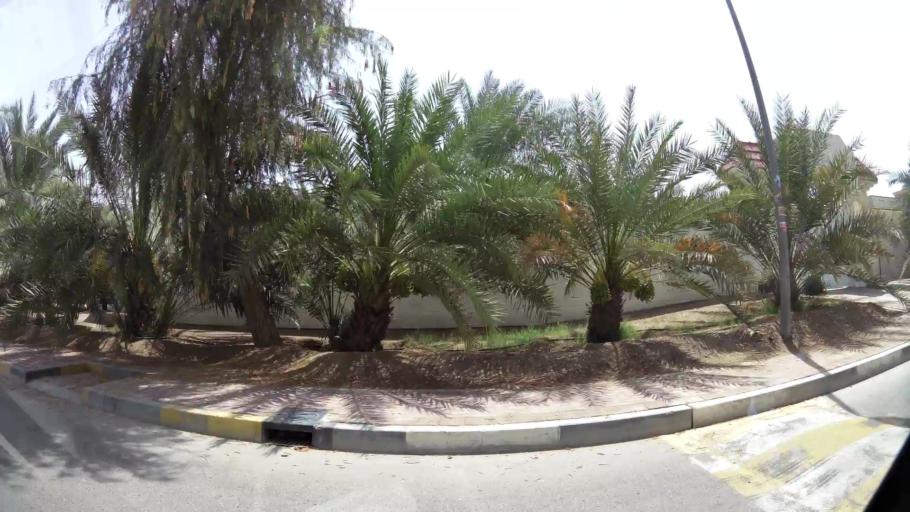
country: AE
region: Abu Dhabi
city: Al Ain
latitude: 24.1794
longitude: 55.7239
